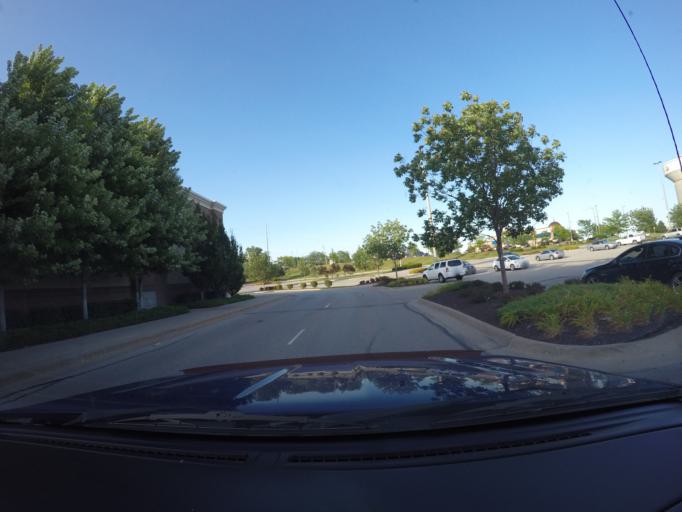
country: US
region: Kansas
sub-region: Wyandotte County
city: Edwardsville
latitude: 39.1271
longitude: -94.8223
